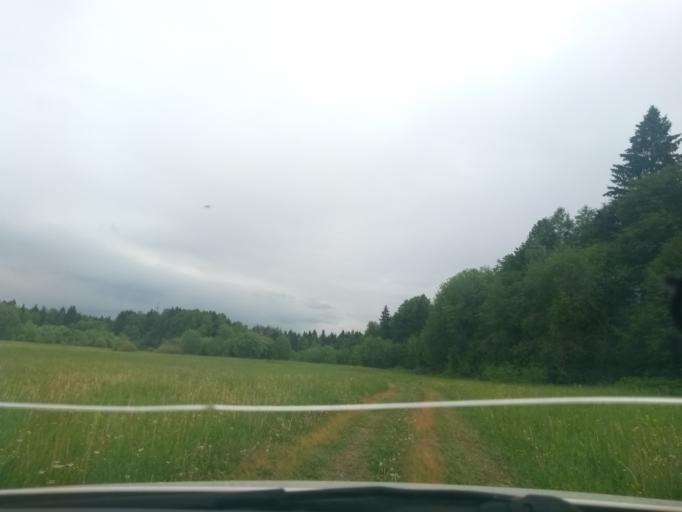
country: RU
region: Perm
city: Ferma
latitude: 57.9798
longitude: 56.3385
